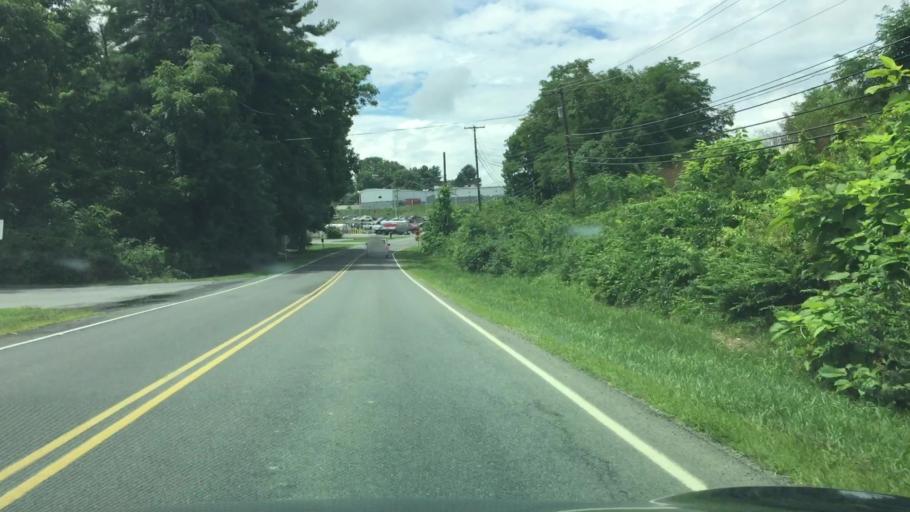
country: US
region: Virginia
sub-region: Wythe County
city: Wytheville
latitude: 36.9476
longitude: -81.0638
